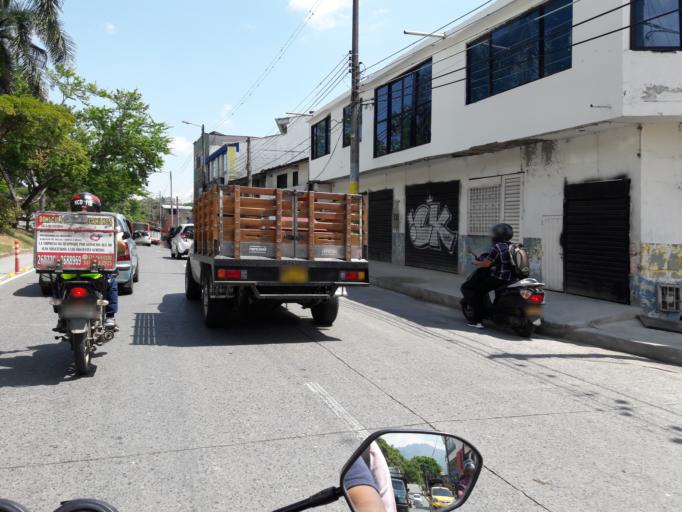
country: CO
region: Tolima
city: Ibague
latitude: 4.4366
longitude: -75.2242
